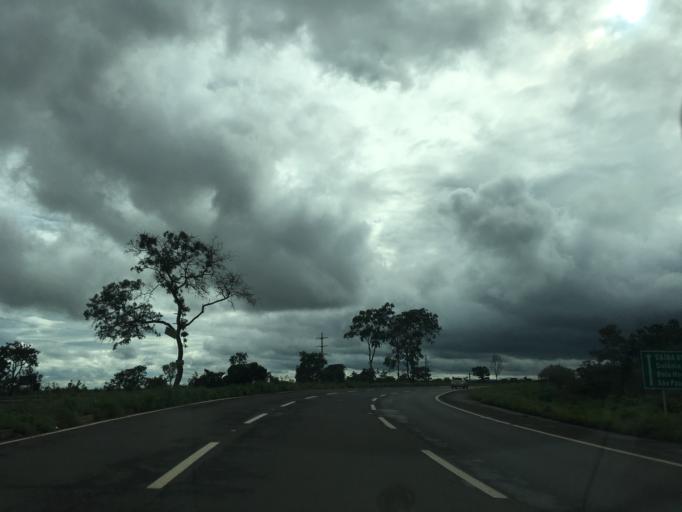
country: BR
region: Federal District
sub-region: Brasilia
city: Brasilia
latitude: -15.9279
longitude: -47.8331
